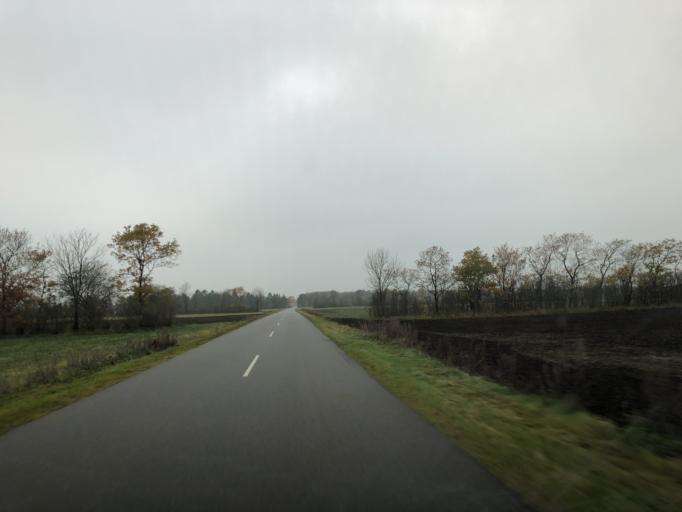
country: DK
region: Central Jutland
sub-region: Herning Kommune
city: Sunds
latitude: 56.2210
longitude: 8.9385
